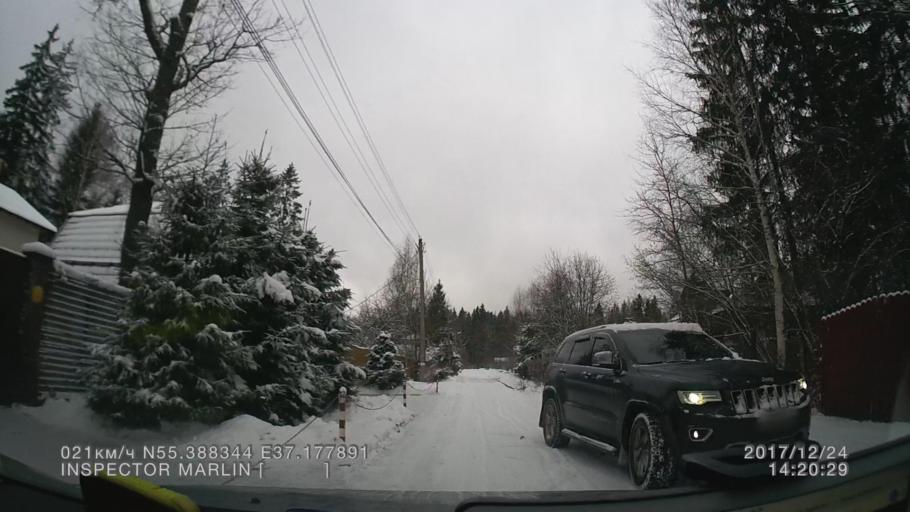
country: RU
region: Moskovskaya
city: Troitsk
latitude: 55.3884
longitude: 37.1778
